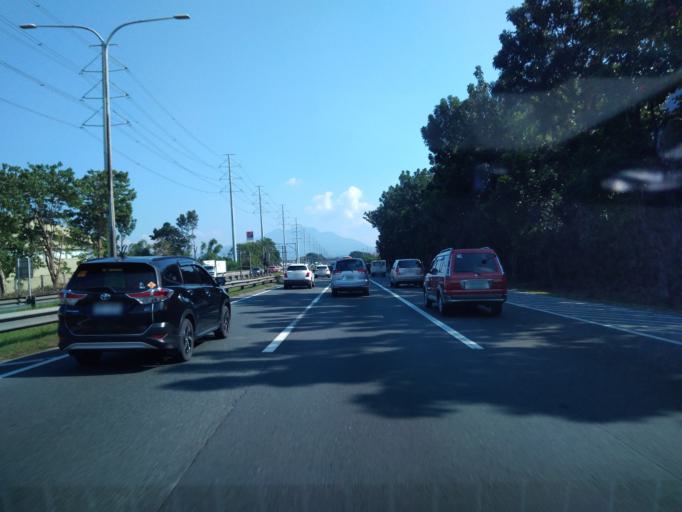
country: PH
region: Calabarzon
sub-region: Province of Laguna
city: Cabuyao
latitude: 14.2384
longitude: 121.1132
